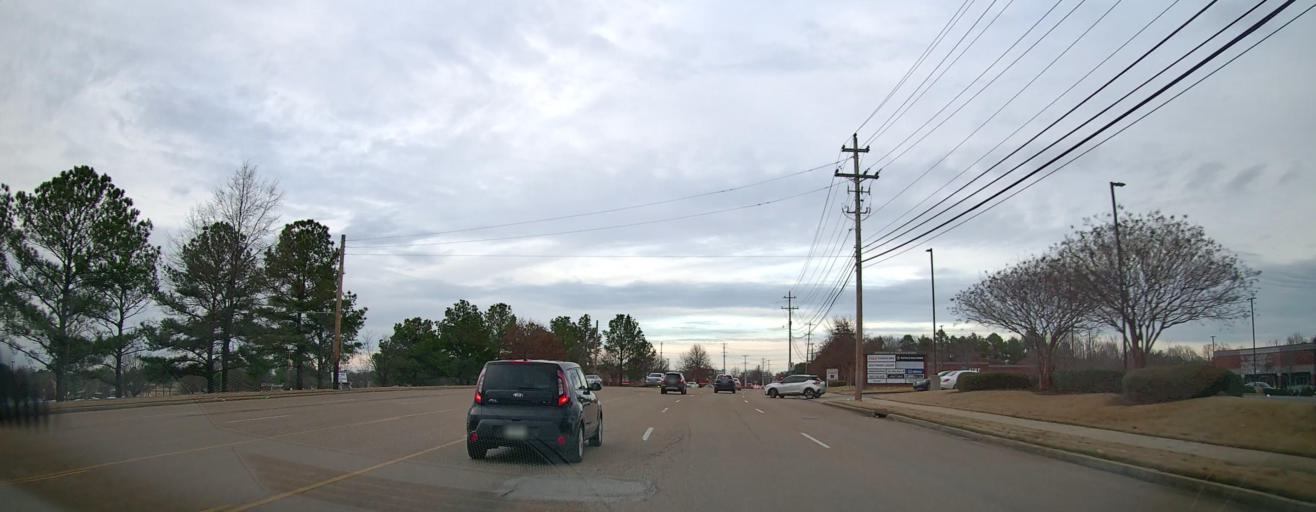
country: US
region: Tennessee
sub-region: Shelby County
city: Germantown
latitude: 35.0459
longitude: -89.7959
